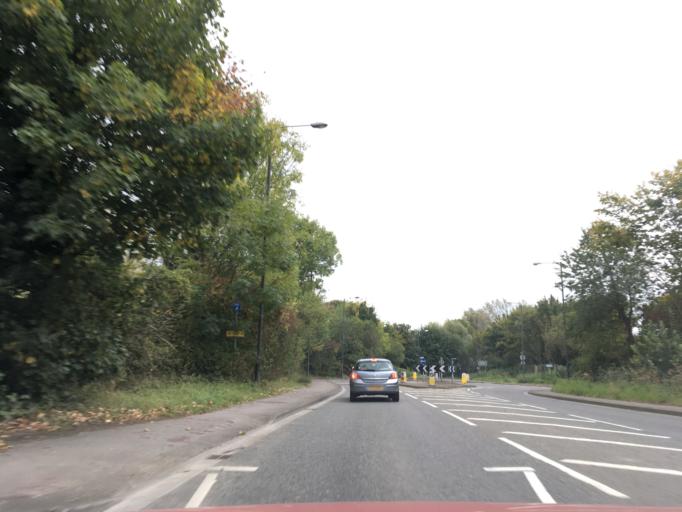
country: GB
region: England
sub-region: Gloucestershire
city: Stonehouse
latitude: 51.7447
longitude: -2.2900
